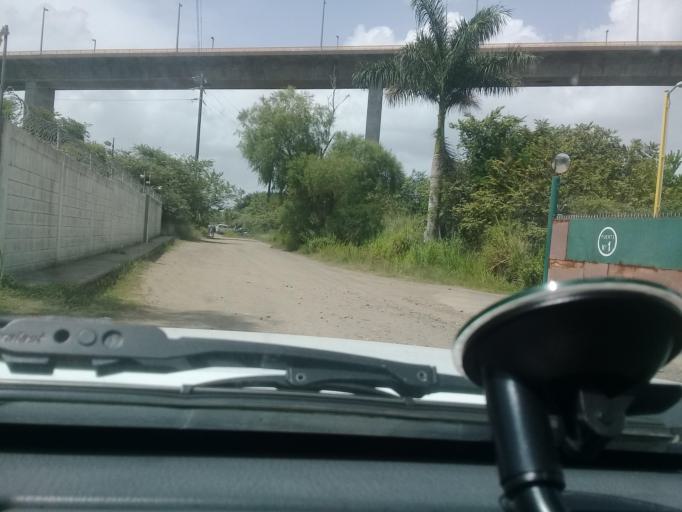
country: MX
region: Veracruz
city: Anahuac
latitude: 22.2270
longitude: -97.8330
